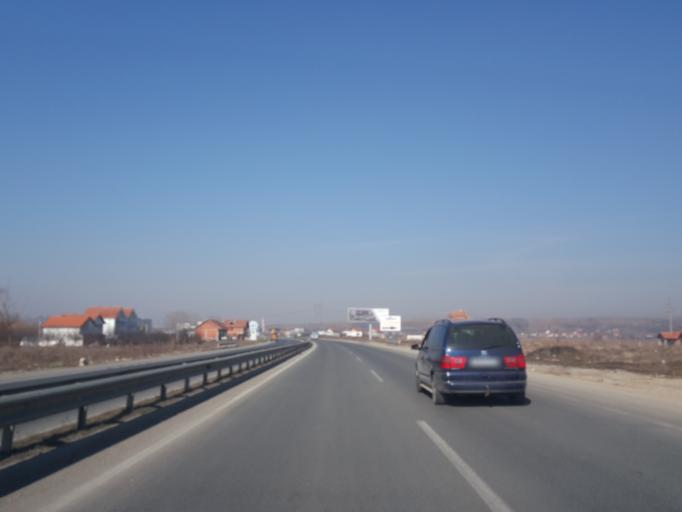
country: XK
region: Pristina
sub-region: Komuna e Obiliqit
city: Obiliq
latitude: 42.7280
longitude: 21.0774
